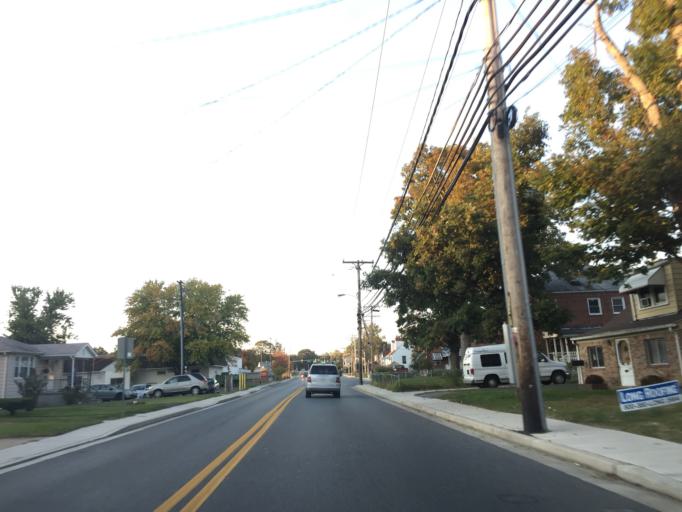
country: US
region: Maryland
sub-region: Baltimore County
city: Essex
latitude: 39.3102
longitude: -76.4648
